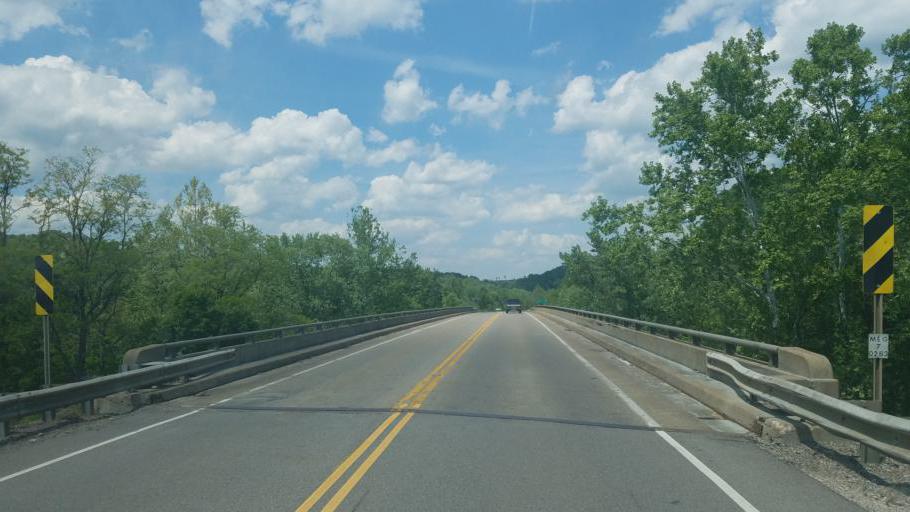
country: US
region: Ohio
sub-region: Meigs County
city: Middleport
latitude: 38.9954
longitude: -82.0763
